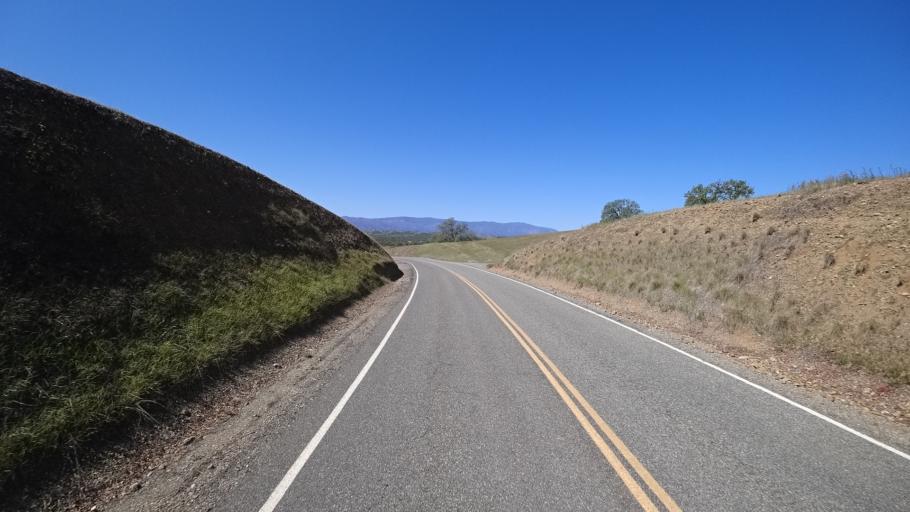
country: US
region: California
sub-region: Tehama County
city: Rancho Tehama Reserve
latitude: 39.8124
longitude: -122.4021
